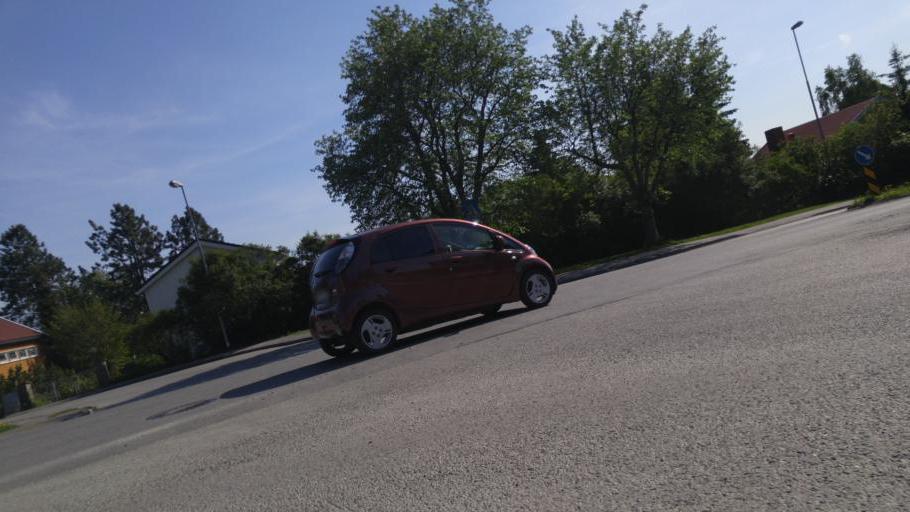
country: NO
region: Sor-Trondelag
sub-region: Trondheim
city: Trondheim
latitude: 63.4170
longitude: 10.4203
